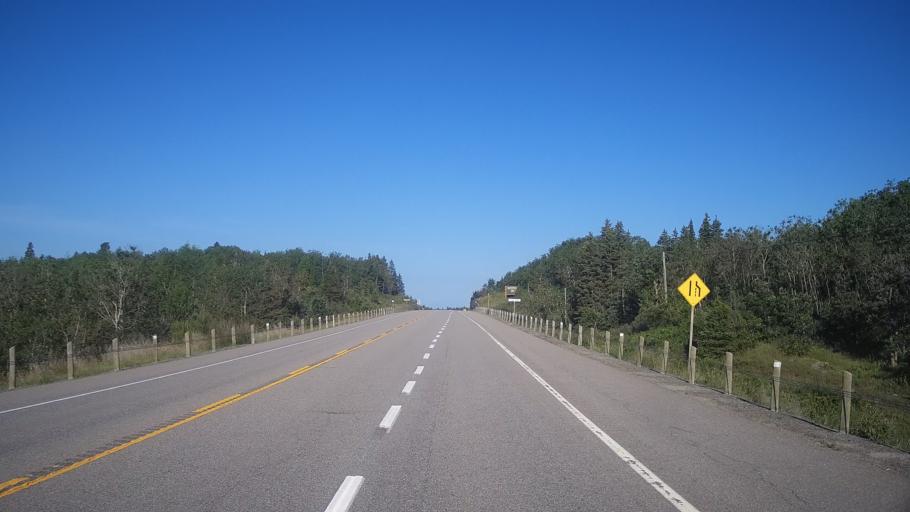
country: US
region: Minnesota
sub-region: Roseau County
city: Warroad
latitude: 49.7170
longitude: -94.7449
